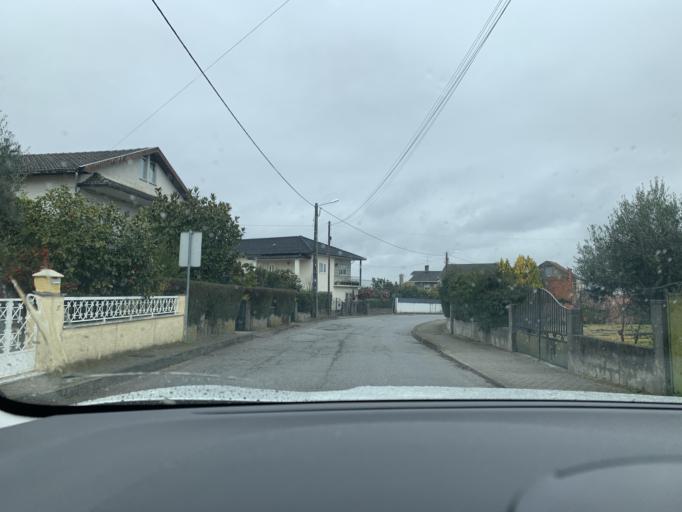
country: PT
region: Viseu
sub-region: Nelas
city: Nelas
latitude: 40.5974
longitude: -7.8432
